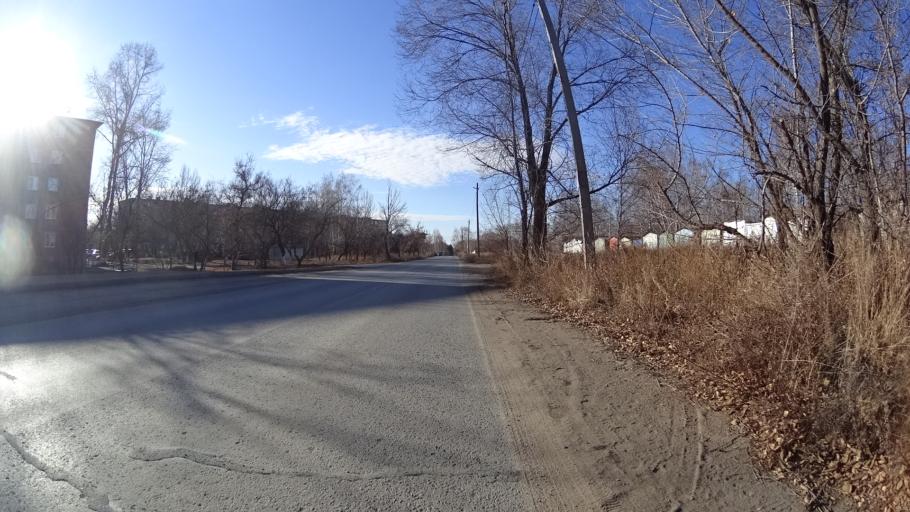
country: RU
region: Chelyabinsk
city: Troitsk
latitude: 54.0531
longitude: 61.6389
